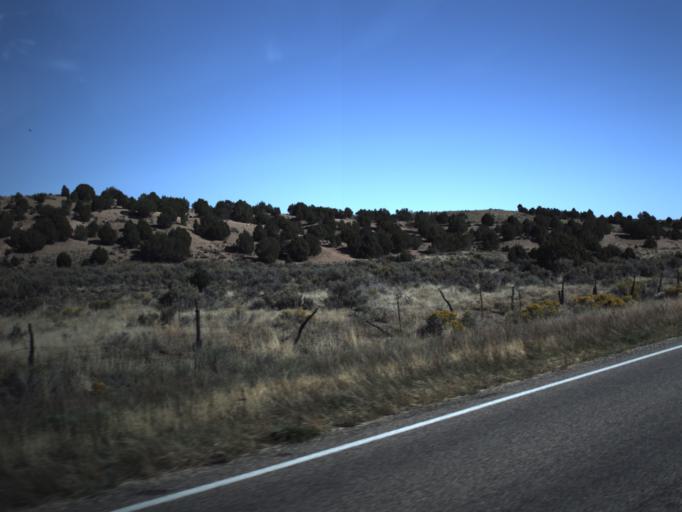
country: US
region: Utah
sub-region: Iron County
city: Cedar City
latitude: 37.6387
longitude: -113.2612
